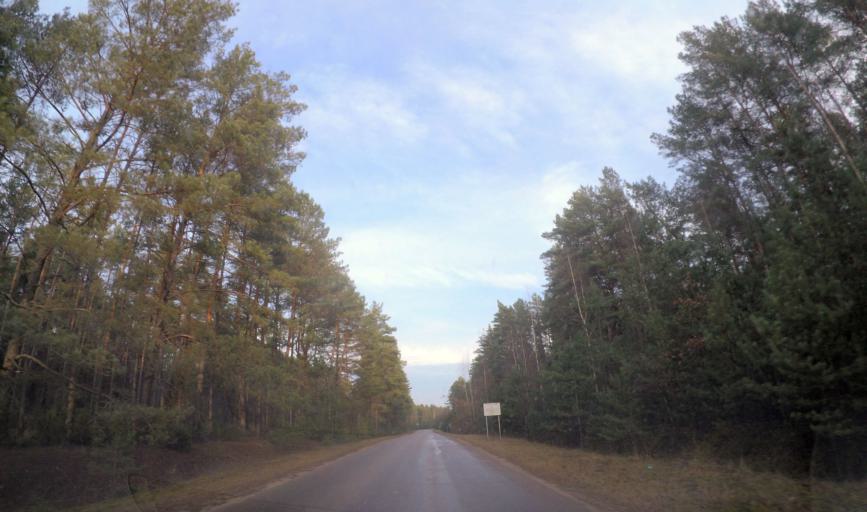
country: LT
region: Alytaus apskritis
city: Druskininkai
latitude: 53.8956
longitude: 24.1397
